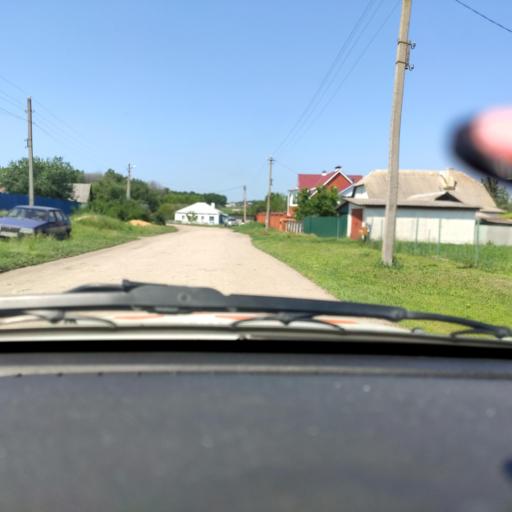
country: RU
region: Voronezj
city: Devitsa
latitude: 51.5963
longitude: 38.9868
